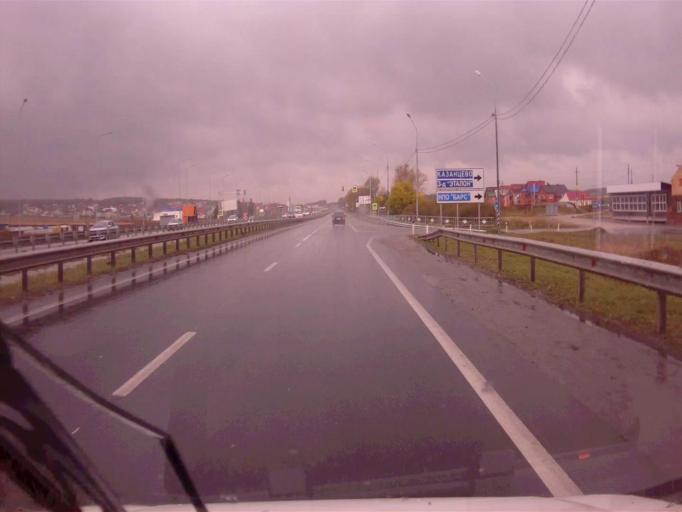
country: RU
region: Chelyabinsk
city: Dolgoderevenskoye
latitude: 55.2730
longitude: 61.3447
